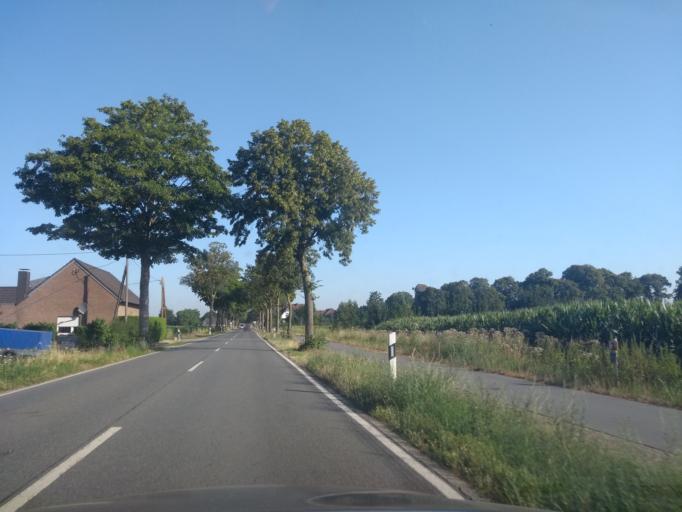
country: DE
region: North Rhine-Westphalia
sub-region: Regierungsbezirk Dusseldorf
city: Kleve
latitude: 51.8201
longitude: 6.1151
